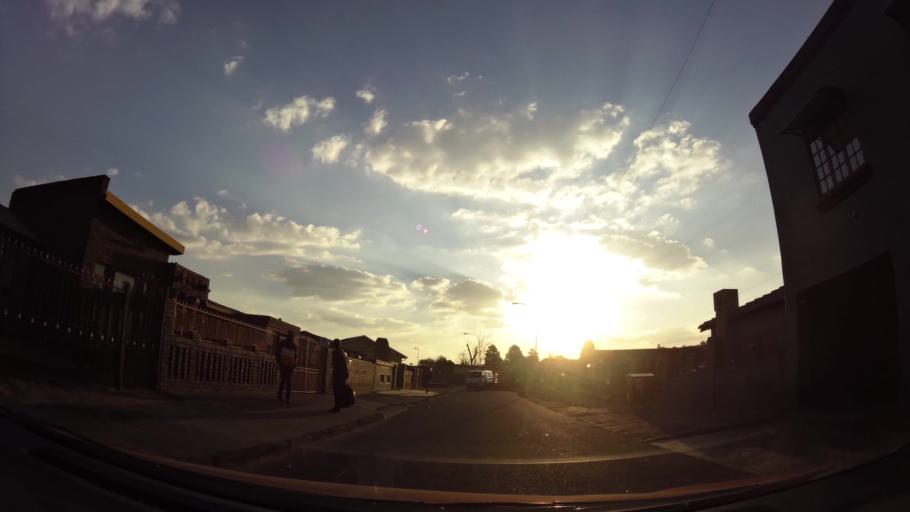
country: ZA
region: Gauteng
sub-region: City of Johannesburg Metropolitan Municipality
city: Roodepoort
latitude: -26.2092
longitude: 27.8995
